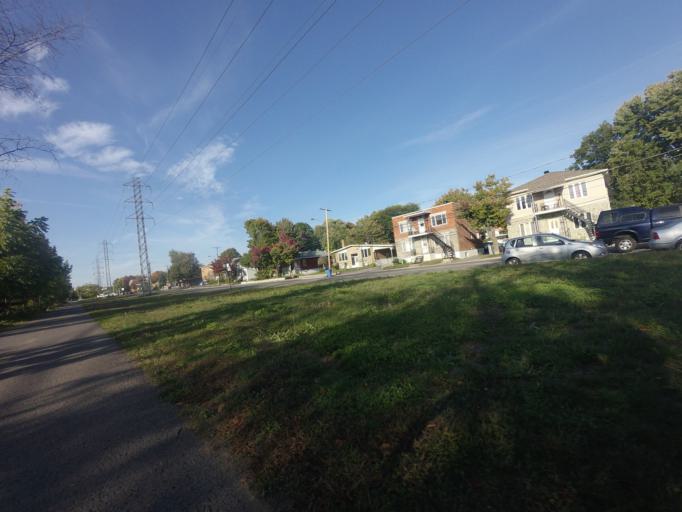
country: CA
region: Quebec
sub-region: Laurentides
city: Saint-Jerome
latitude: 45.7854
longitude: -73.9966
